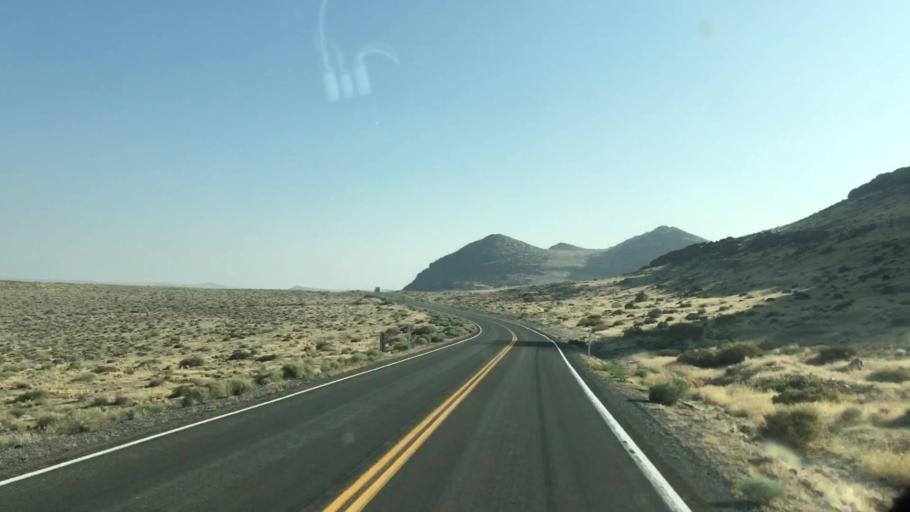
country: US
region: Nevada
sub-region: Lyon County
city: Fernley
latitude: 39.8720
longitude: -119.3963
